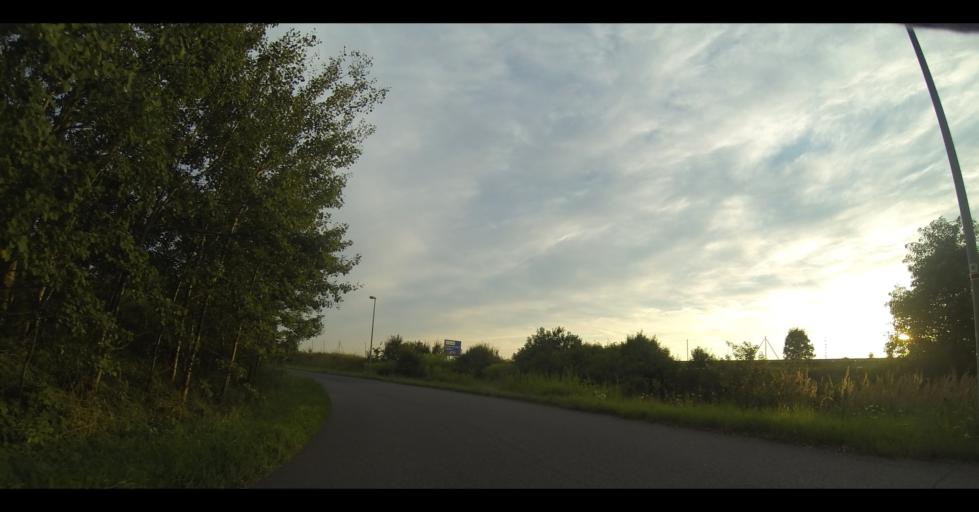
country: DE
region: Saxony
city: Albertstadt
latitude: 51.1254
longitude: 13.7485
